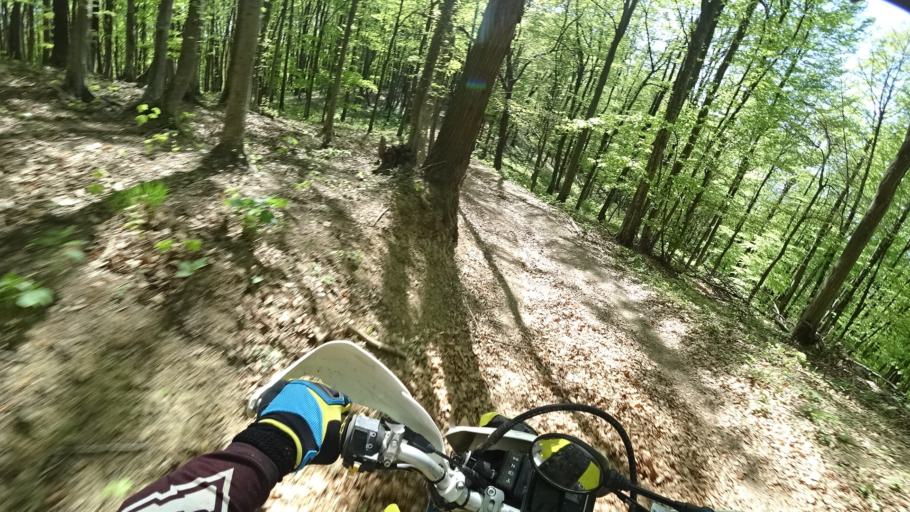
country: HR
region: Zagrebacka
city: Jablanovec
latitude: 45.8857
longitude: 15.9059
